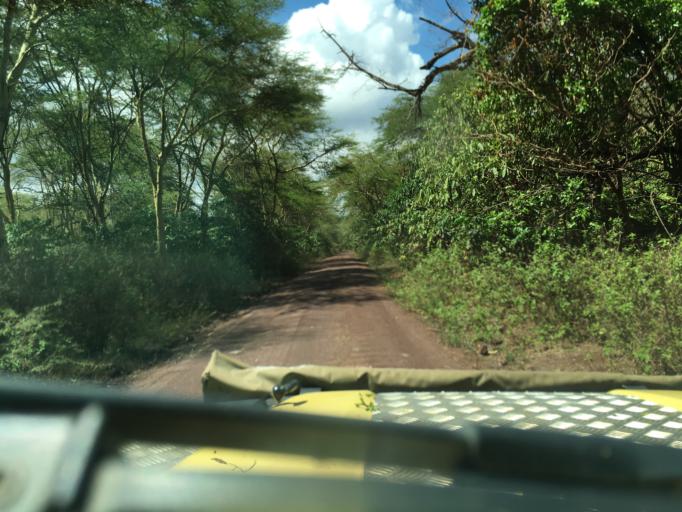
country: TZ
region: Arusha
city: Mto wa Mbu
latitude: -3.4069
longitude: 35.8242
